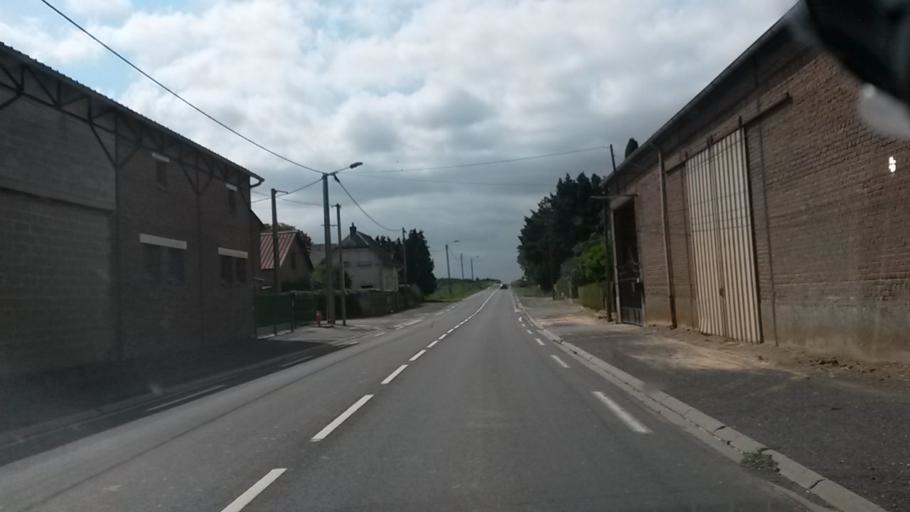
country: FR
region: Nord-Pas-de-Calais
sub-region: Departement du Pas-de-Calais
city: Vaulx-Vraucourt
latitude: 50.1186
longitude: 2.9282
